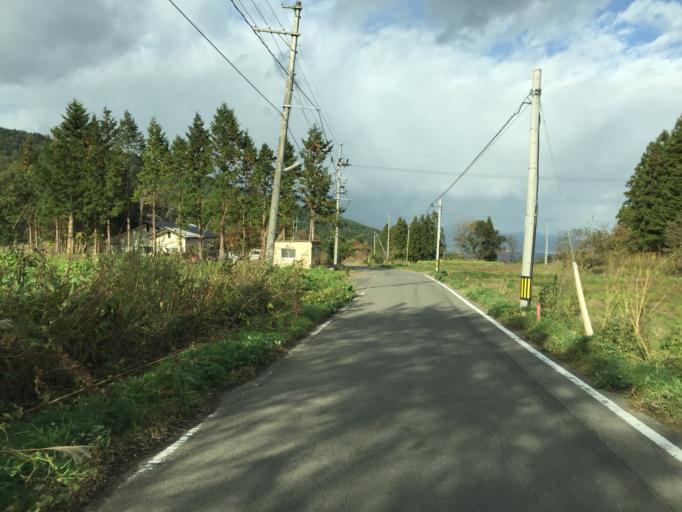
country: JP
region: Fukushima
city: Fukushima-shi
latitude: 37.7104
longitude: 140.3415
